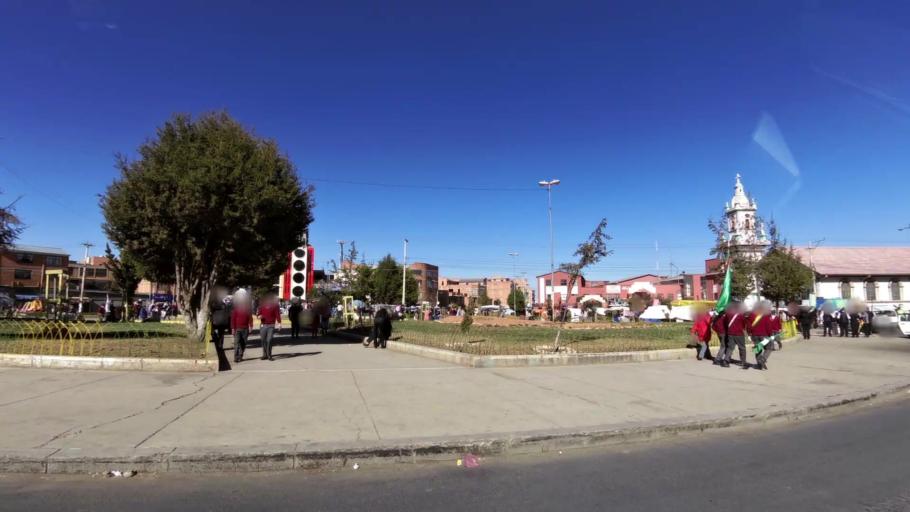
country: BO
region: La Paz
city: La Paz
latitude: -16.5248
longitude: -68.2004
